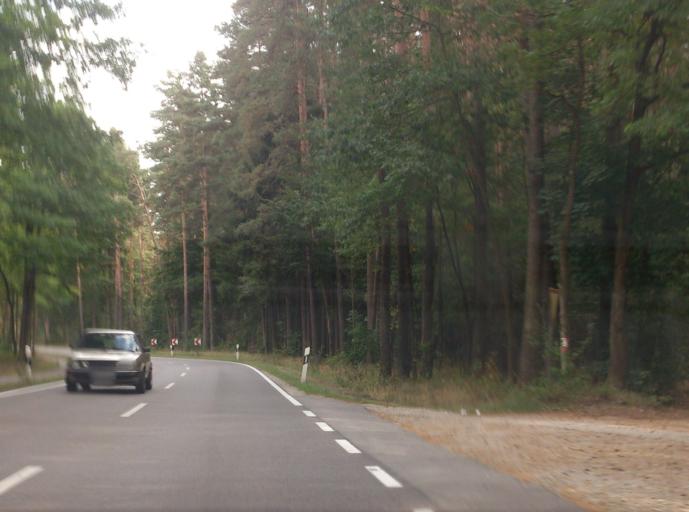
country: DE
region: Bavaria
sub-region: Regierungsbezirk Mittelfranken
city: Wetzendorf
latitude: 49.5285
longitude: 11.0694
